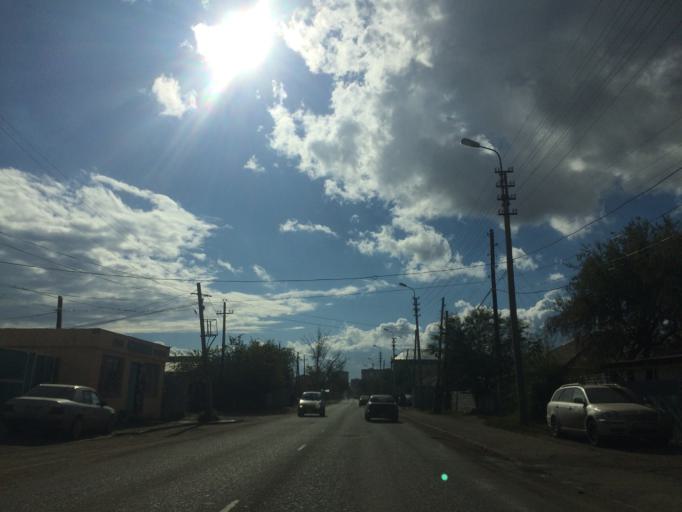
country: KZ
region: Astana Qalasy
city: Astana
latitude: 51.1891
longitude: 71.3850
